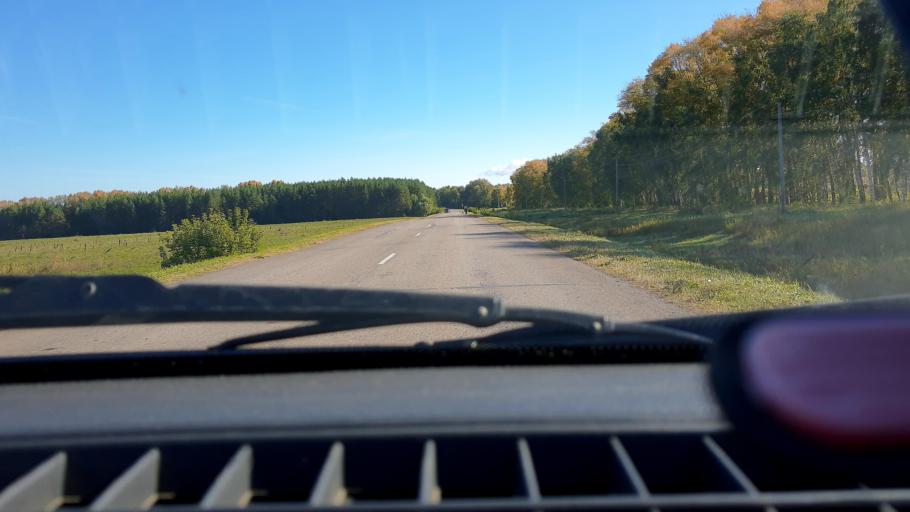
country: RU
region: Bashkortostan
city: Kushnarenkovo
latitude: 55.0614
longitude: 55.4390
